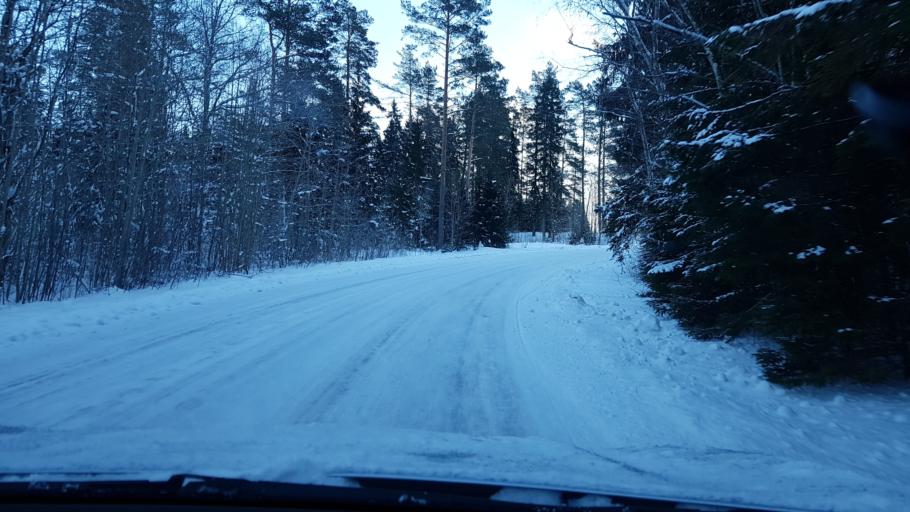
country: EE
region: Harju
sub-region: Nissi vald
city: Turba
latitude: 59.1445
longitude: 24.1573
